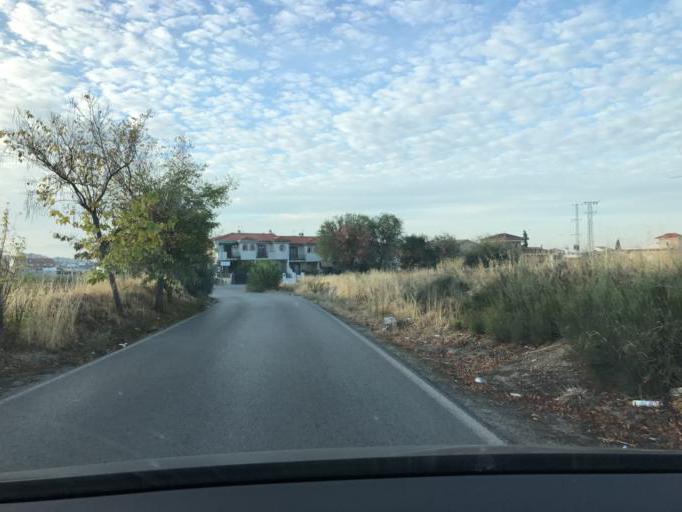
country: ES
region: Andalusia
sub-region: Provincia de Granada
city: Pulianas
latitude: 37.2203
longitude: -3.6019
